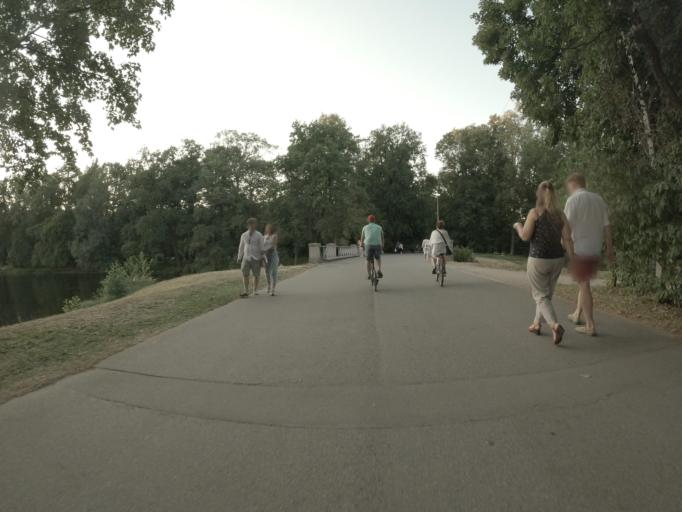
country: RU
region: Leningrad
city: Krestovskiy ostrov
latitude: 59.9785
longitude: 30.2531
